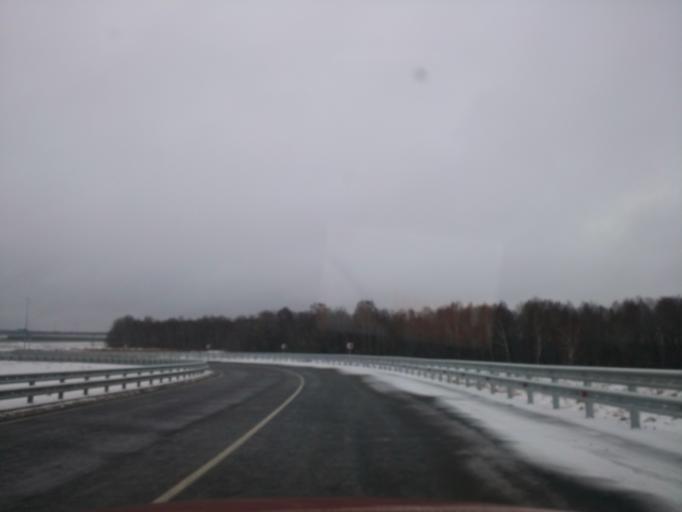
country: RU
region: Tverskaya
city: Likhoslavl'
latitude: 56.9809
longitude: 35.4197
